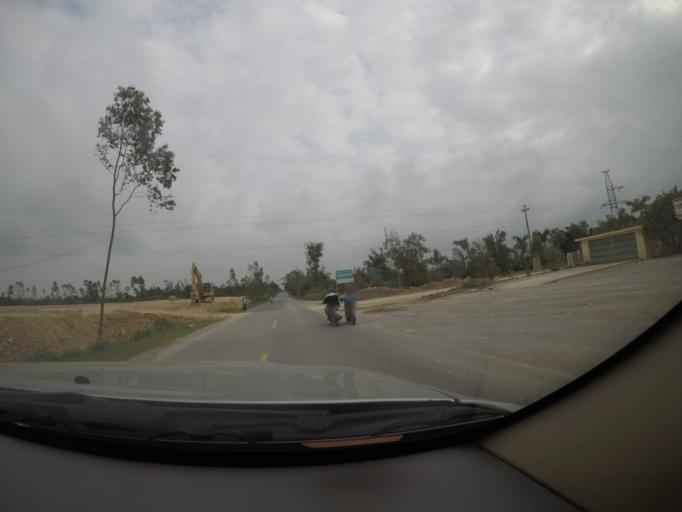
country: VN
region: Quang Binh
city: Quan Hau
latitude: 17.4151
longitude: 106.5986
